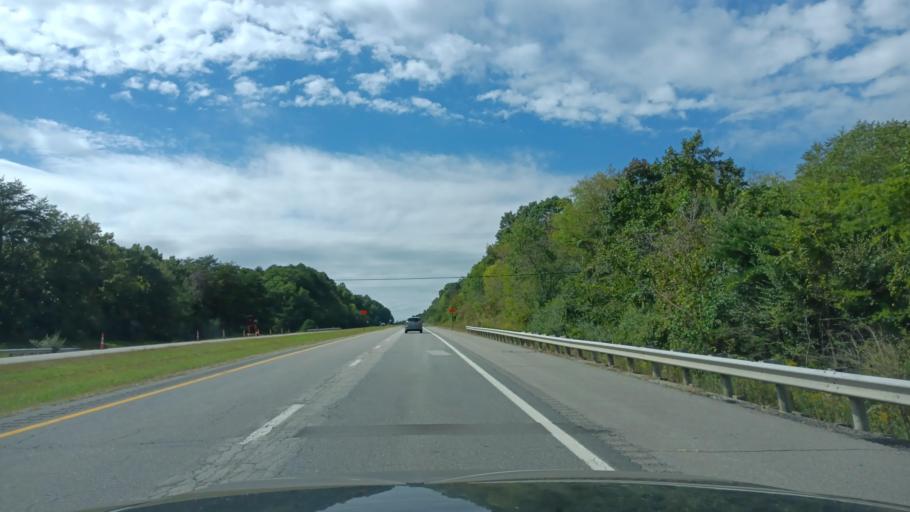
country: US
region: West Virginia
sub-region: Ritchie County
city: Harrisville
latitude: 39.2611
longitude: -81.1446
